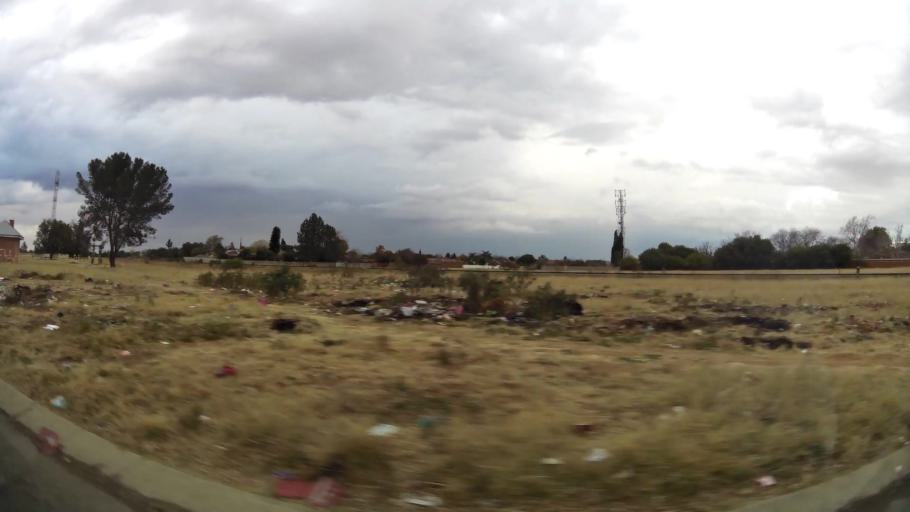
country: ZA
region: Orange Free State
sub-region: Lejweleputswa District Municipality
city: Welkom
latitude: -27.9555
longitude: 26.7232
